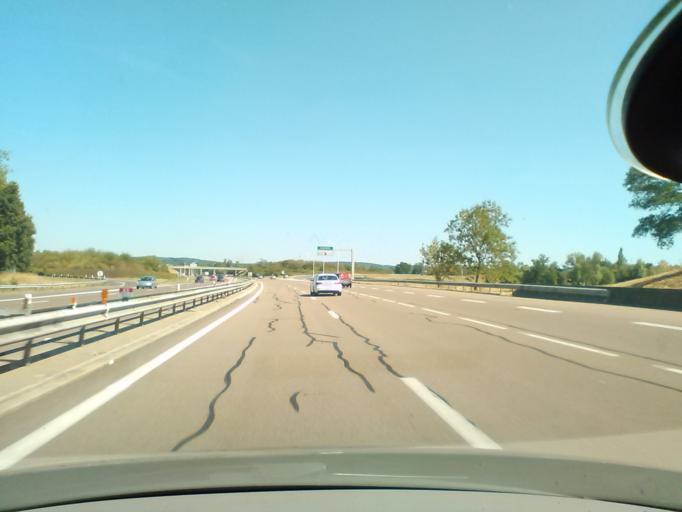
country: FR
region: Bourgogne
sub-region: Departement de l'Yonne
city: Gurgy
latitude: 47.8567
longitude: 3.5429
